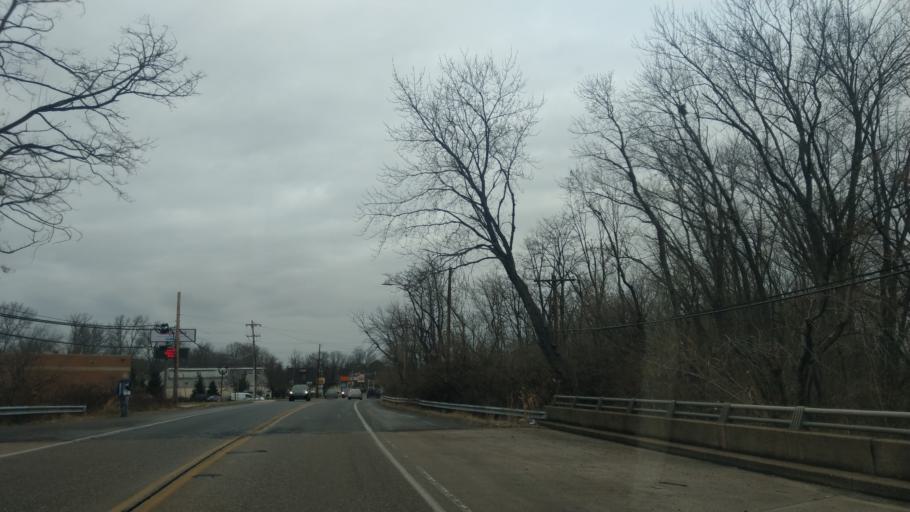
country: US
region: Pennsylvania
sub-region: Bucks County
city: Hulmeville
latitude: 40.1390
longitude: -74.8747
